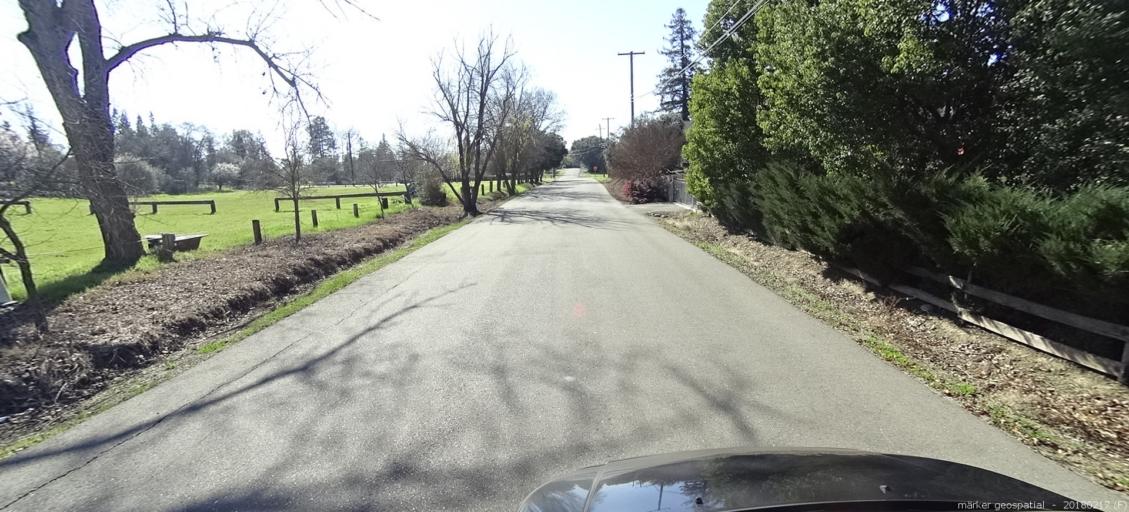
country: US
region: California
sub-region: Sacramento County
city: Orangevale
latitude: 38.7124
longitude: -121.2209
